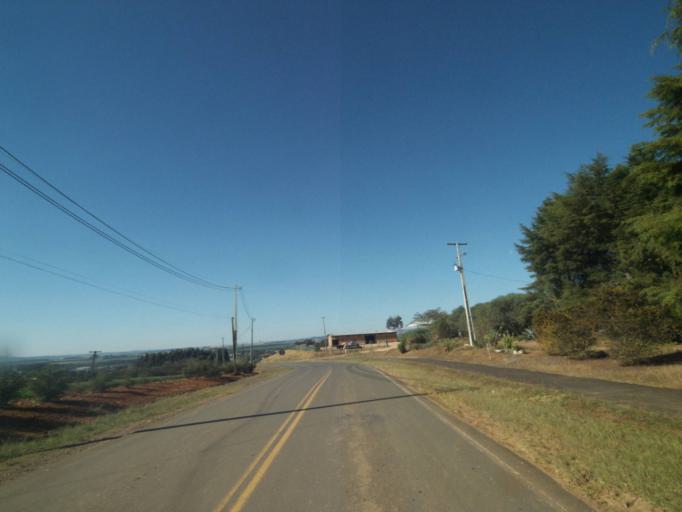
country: BR
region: Parana
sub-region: Tibagi
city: Tibagi
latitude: -24.5229
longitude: -50.4310
